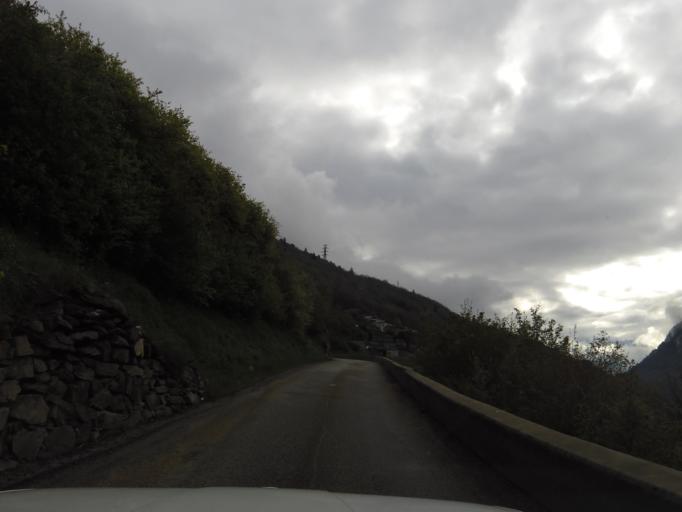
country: FR
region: Rhone-Alpes
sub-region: Departement de la Savoie
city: Saint-Michel-de-Maurienne
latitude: 45.2099
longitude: 6.5285
